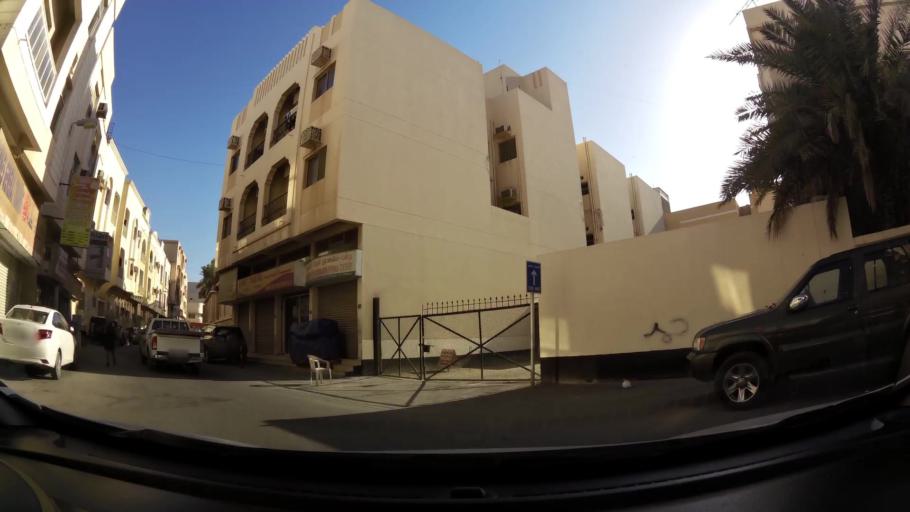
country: BH
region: Manama
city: Manama
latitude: 26.2334
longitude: 50.5857
